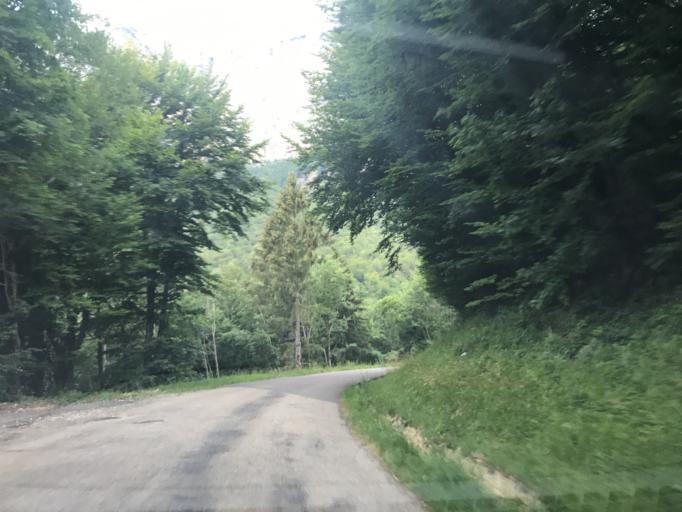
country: FR
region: Rhone-Alpes
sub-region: Departement de l'Isere
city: Saint-Vincent-de-Mercuze
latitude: 45.3790
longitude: 5.9264
